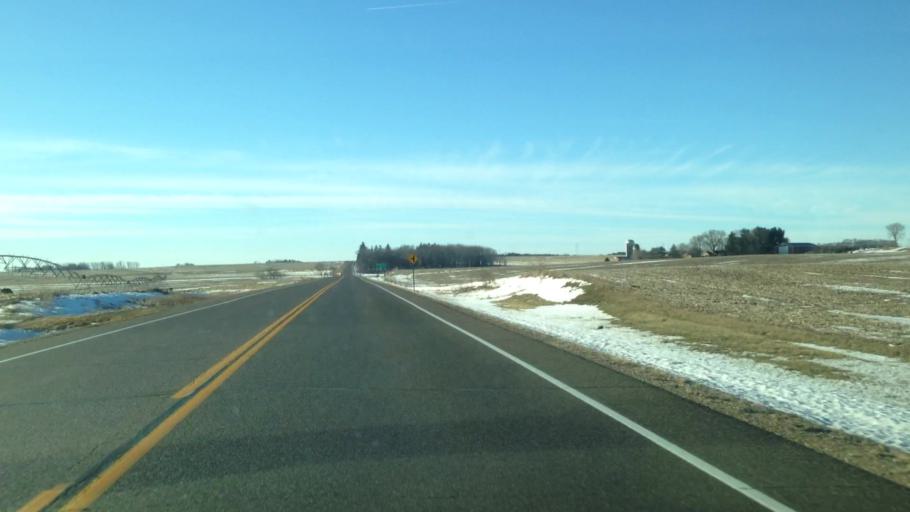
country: US
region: Minnesota
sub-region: Dakota County
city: Farmington
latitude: 44.5753
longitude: -93.0287
